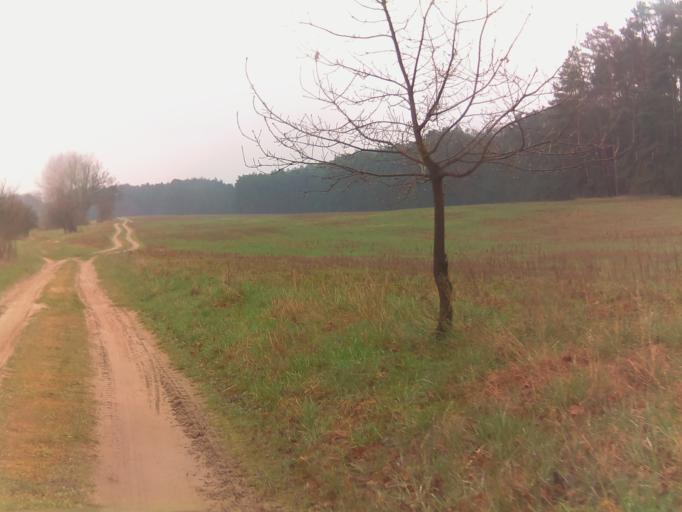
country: DE
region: Brandenburg
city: Lieberose
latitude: 52.0122
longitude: 14.2159
